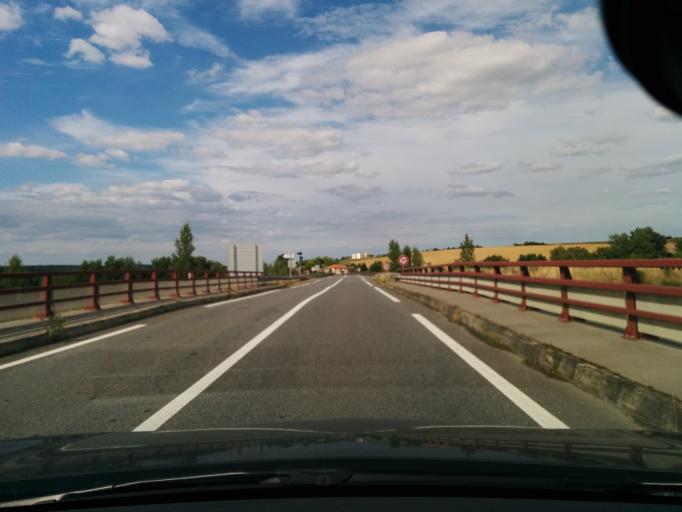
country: FR
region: Midi-Pyrenees
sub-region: Departement du Gers
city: Aubiet
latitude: 43.6547
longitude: 0.7834
